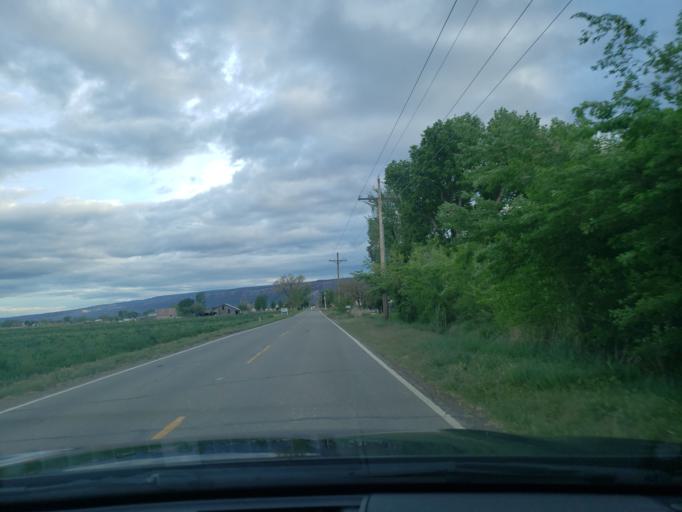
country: US
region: Colorado
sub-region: Mesa County
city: Fruita
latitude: 39.1712
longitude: -108.7012
